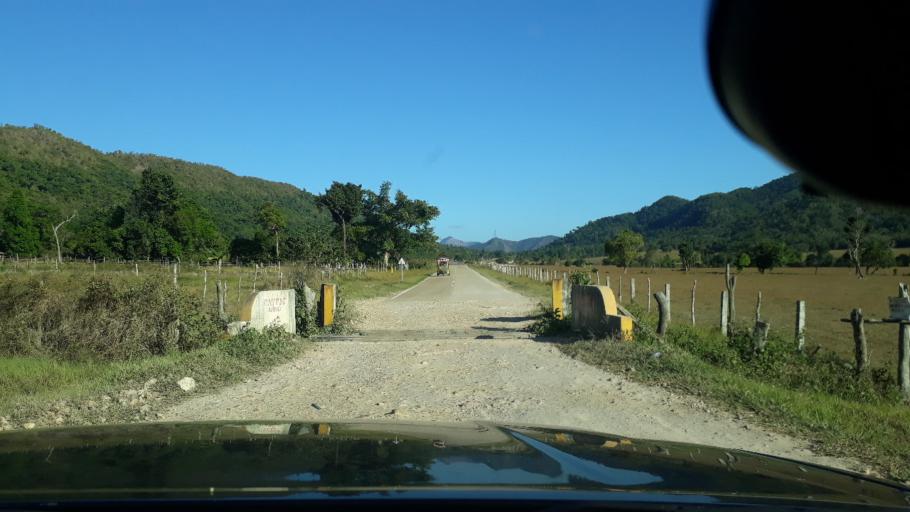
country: PH
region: Mimaropa
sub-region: Province of Palawan
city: Coron
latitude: 12.0903
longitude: 120.1287
